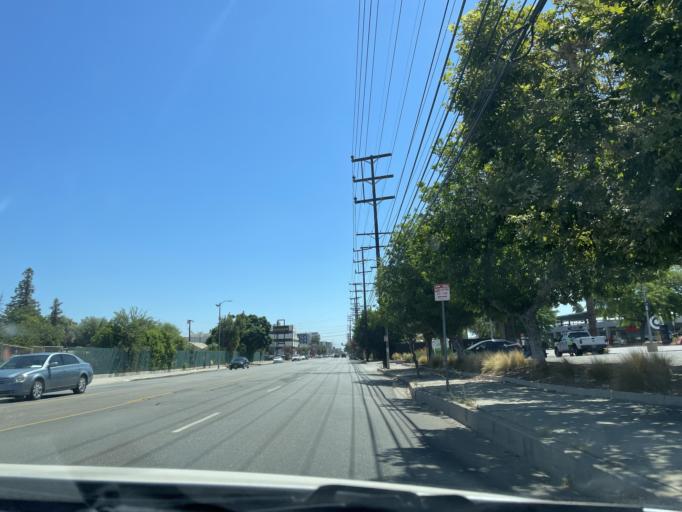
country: US
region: California
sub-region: Los Angeles County
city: Canoga Park
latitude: 34.1937
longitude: -118.6044
